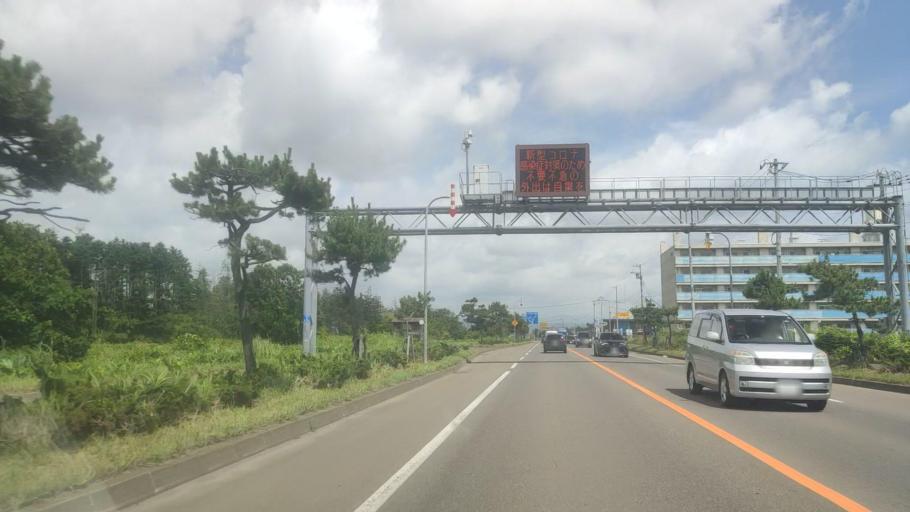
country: JP
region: Hokkaido
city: Niseko Town
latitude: 42.4982
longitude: 140.3643
